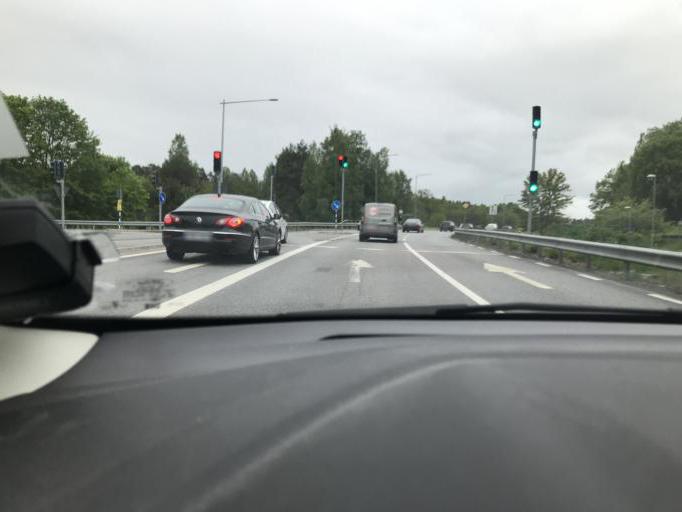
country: SE
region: Stockholm
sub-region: Botkyrka Kommun
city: Alby
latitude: 59.2334
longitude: 17.8428
